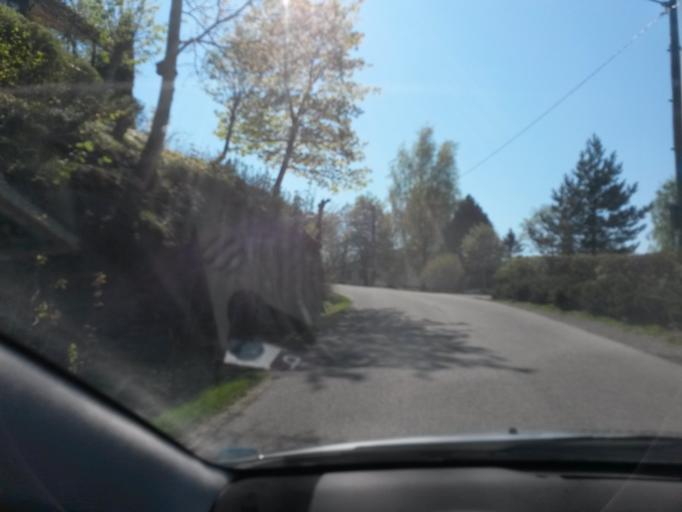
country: NO
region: Akershus
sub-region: Asker
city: Asker
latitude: 59.8348
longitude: 10.4095
